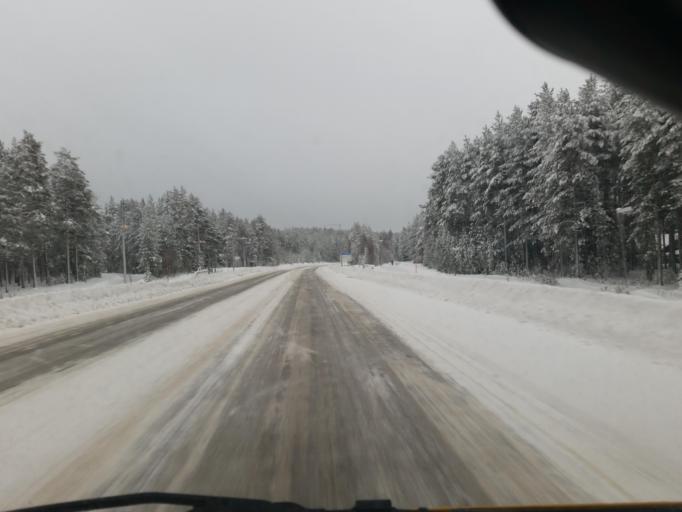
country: SE
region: Norrbotten
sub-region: Pitea Kommun
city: Pitea
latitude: 65.2715
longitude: 21.5266
